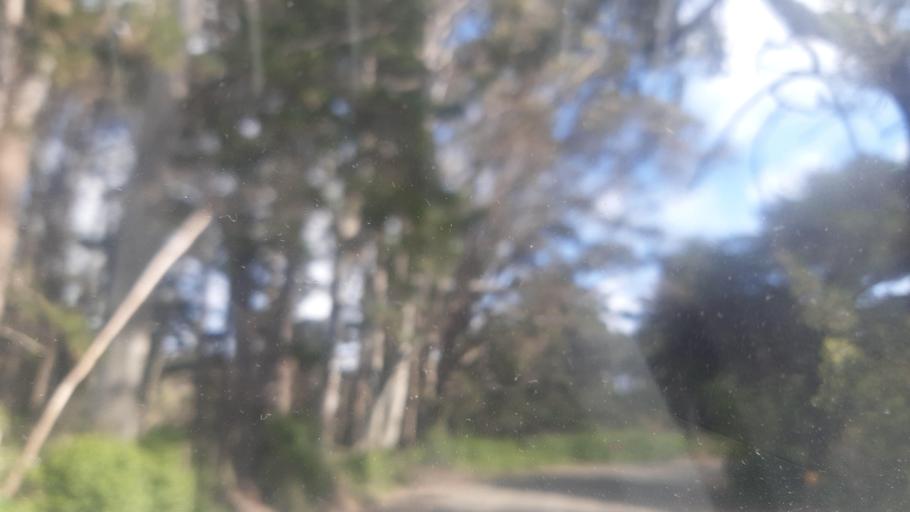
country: NZ
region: Northland
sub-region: Far North District
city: Kaitaia
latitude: -34.7548
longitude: 173.0476
